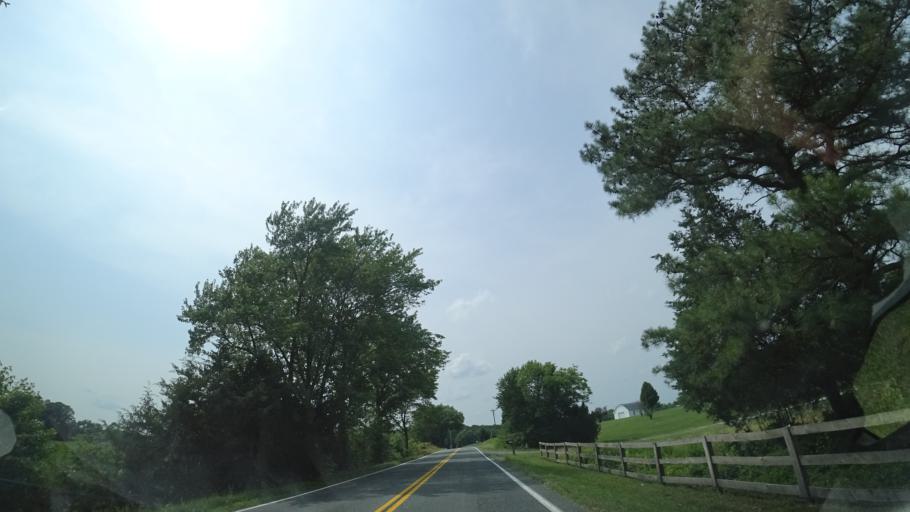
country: US
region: Virginia
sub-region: Spotsylvania County
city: Spotsylvania Courthouse
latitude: 38.1369
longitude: -77.5370
